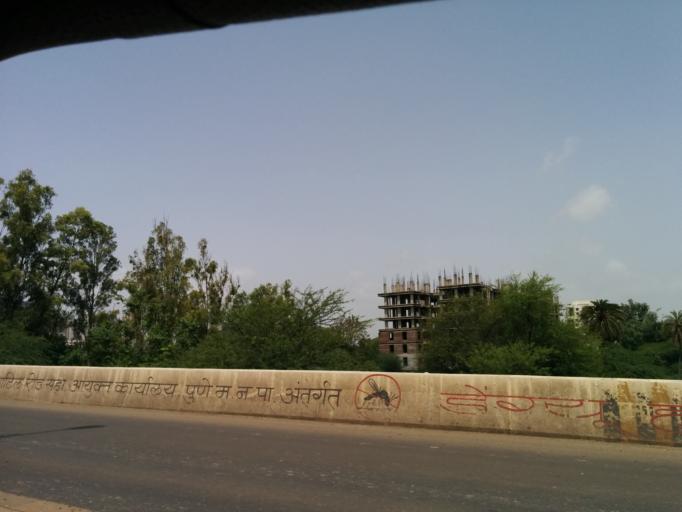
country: IN
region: Maharashtra
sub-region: Pune Division
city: Lohogaon
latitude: 18.5279
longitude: 73.9323
